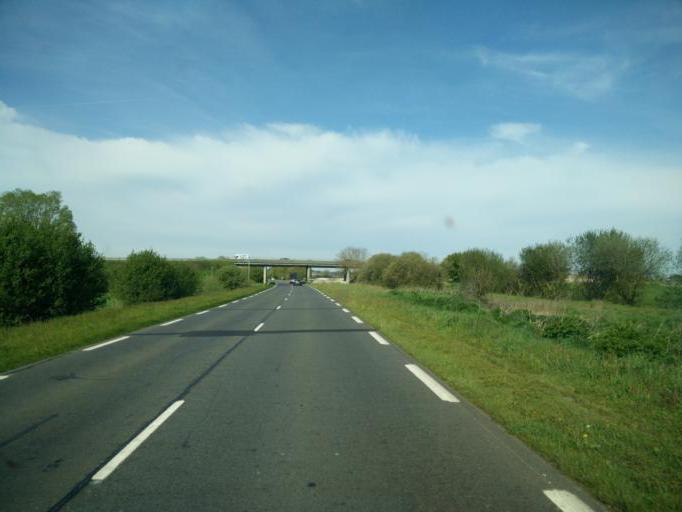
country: FR
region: Lower Normandy
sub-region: Departement de la Manche
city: Pontorson
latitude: 48.5624
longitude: -1.5077
